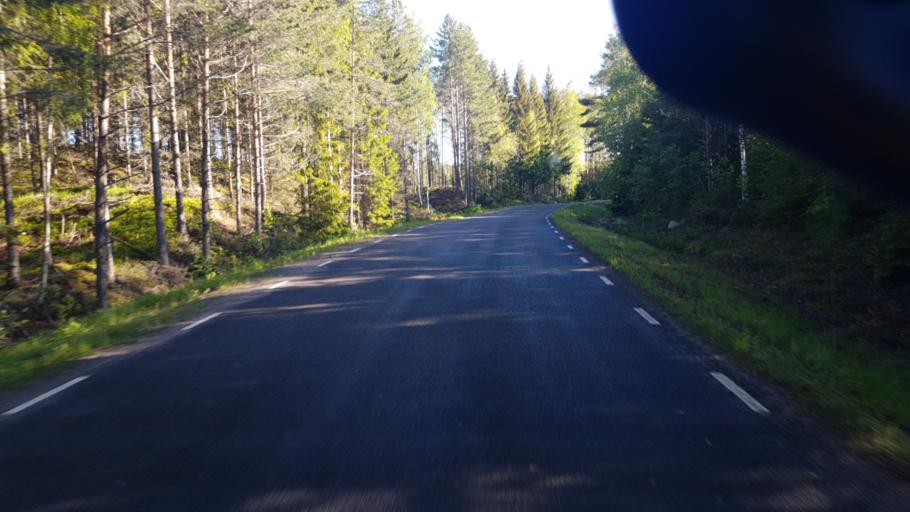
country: SE
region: Vaermland
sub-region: Arvika Kommun
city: Arvika
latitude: 59.5415
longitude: 12.3975
